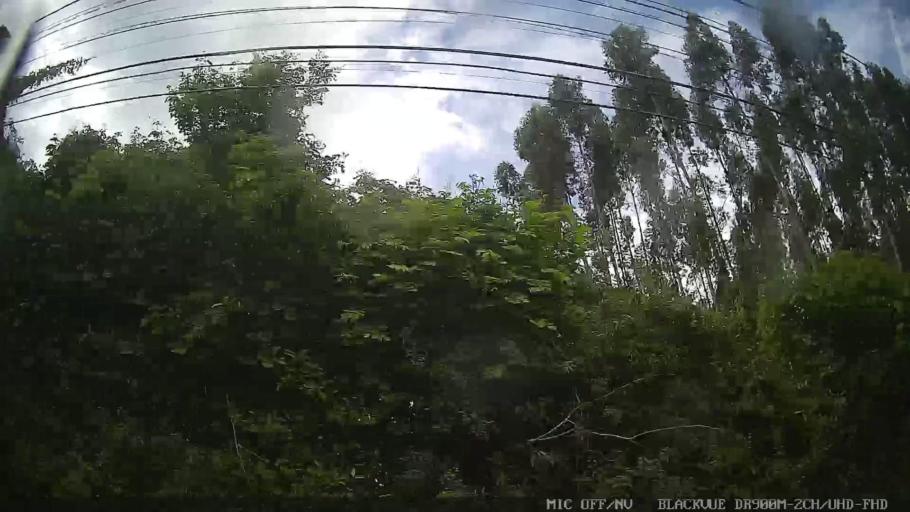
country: BR
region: Sao Paulo
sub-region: Serra Negra
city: Serra Negra
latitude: -22.6178
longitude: -46.7311
